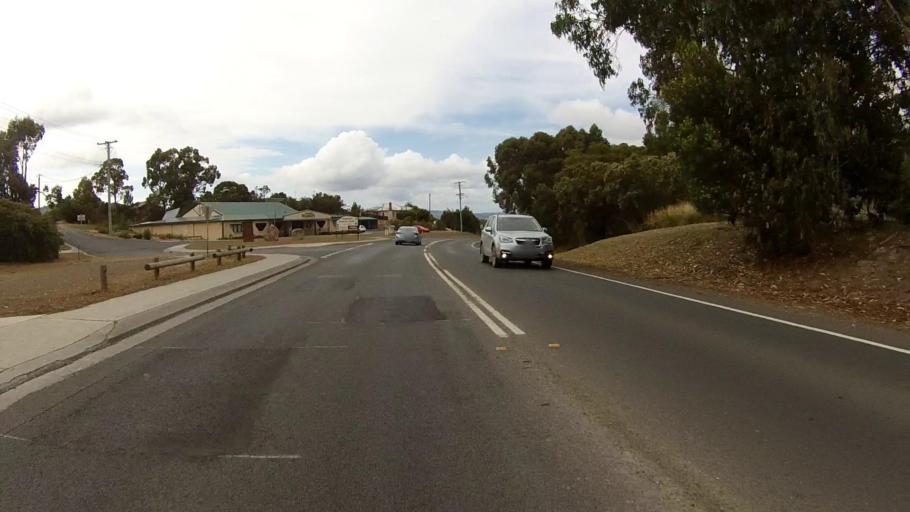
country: AU
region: Tasmania
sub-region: Kingborough
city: Margate
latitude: -43.0293
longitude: 147.2635
